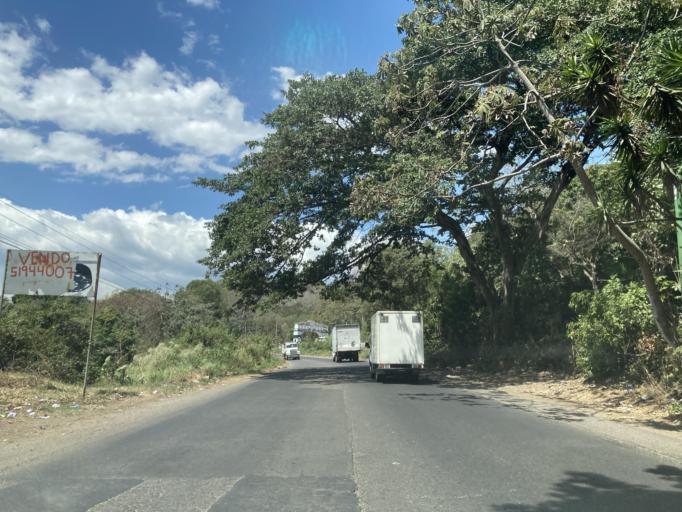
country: GT
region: Santa Rosa
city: Cuilapa
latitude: 14.2768
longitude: -90.3106
